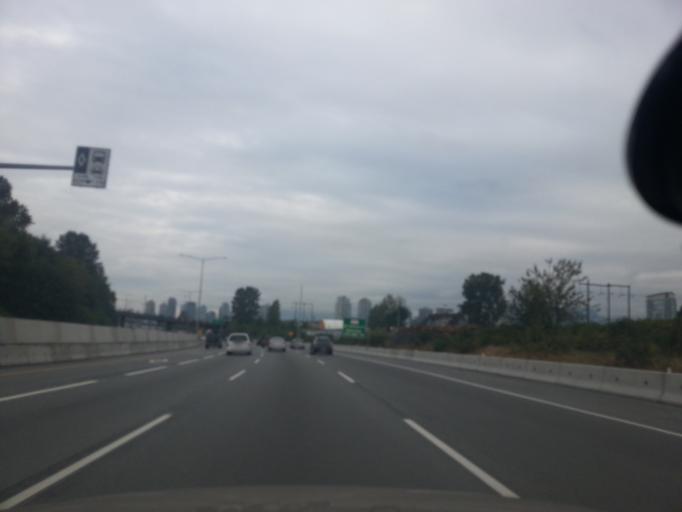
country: CA
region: British Columbia
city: Burnaby
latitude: 49.2563
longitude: -122.9795
